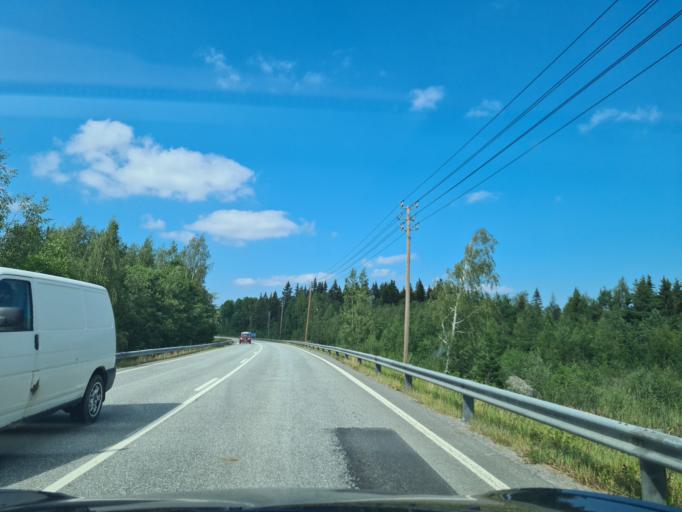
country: FI
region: Ostrobothnia
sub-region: Vaasa
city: Vaasa
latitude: 63.1892
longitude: 21.5648
